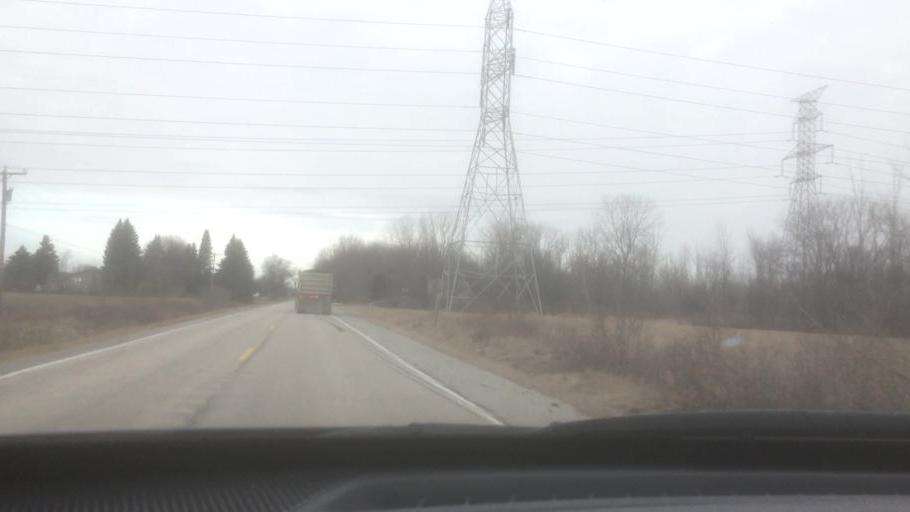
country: US
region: Michigan
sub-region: Bay County
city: Essexville
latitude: 43.5221
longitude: -83.7912
